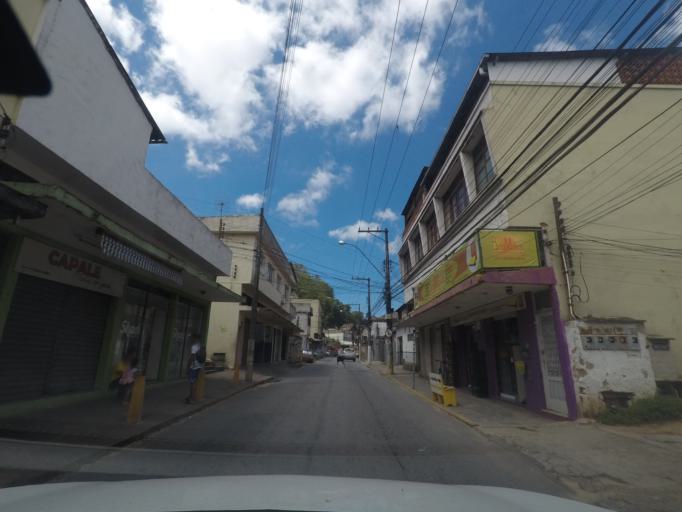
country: BR
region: Rio de Janeiro
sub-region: Teresopolis
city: Teresopolis
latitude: -22.4038
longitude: -42.9767
